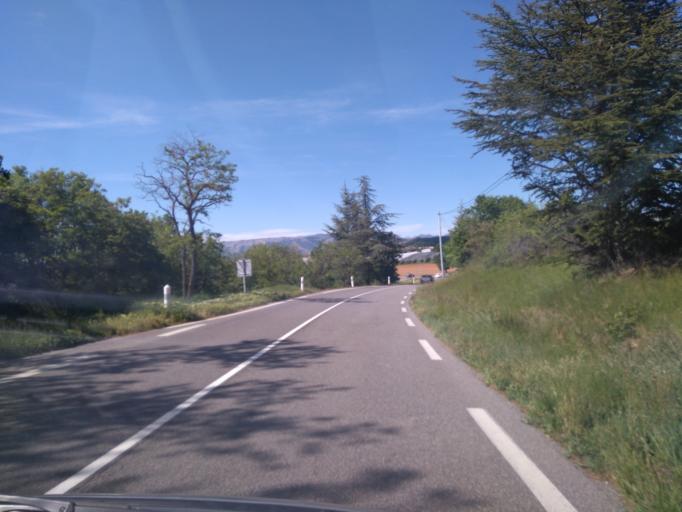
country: FR
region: Provence-Alpes-Cote d'Azur
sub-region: Departement des Hautes-Alpes
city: Laragne-Monteglin
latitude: 44.2728
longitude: 5.8536
